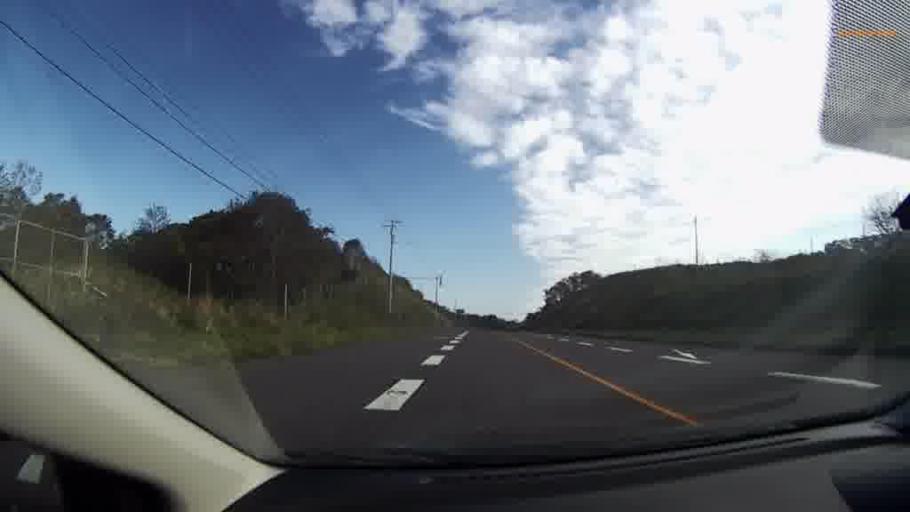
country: JP
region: Hokkaido
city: Kushiro
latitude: 42.9057
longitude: 143.9699
